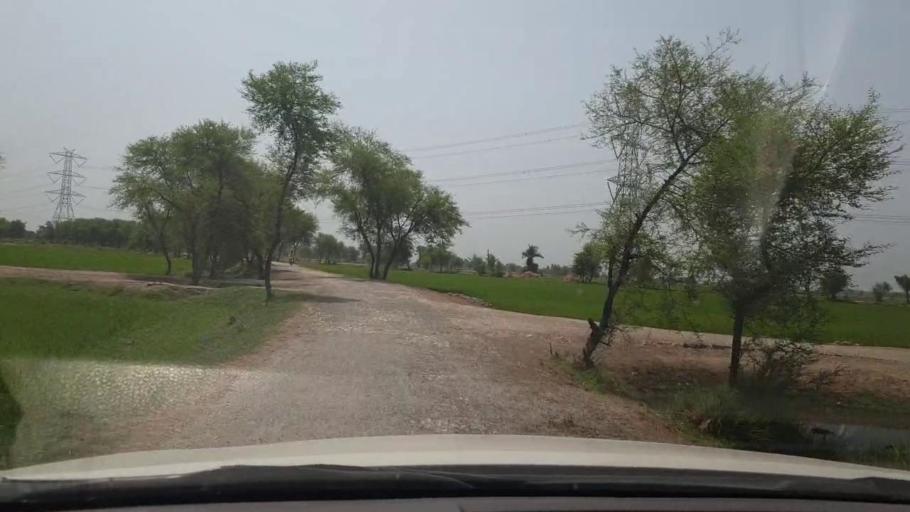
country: PK
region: Sindh
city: Shikarpur
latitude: 28.0181
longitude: 68.6488
